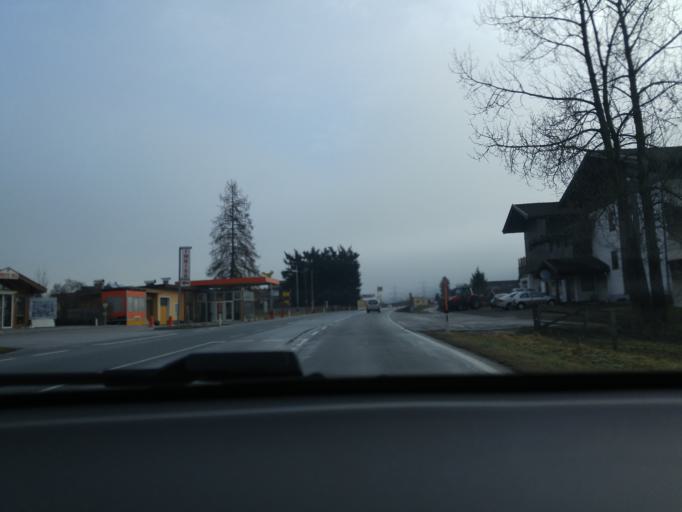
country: AT
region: Salzburg
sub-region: Politischer Bezirk Zell am See
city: Niedernsill
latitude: 47.2844
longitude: 12.6208
